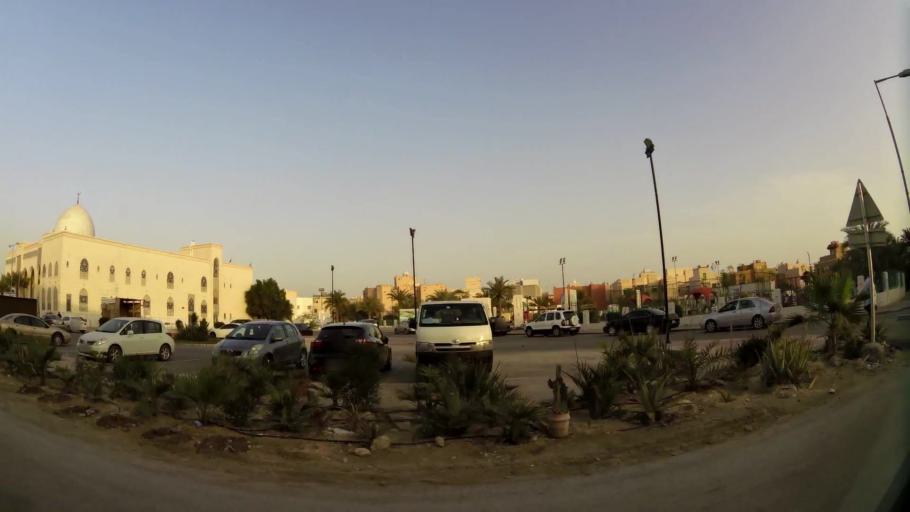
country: BH
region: Northern
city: Madinat `Isa
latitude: 26.1836
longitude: 50.4745
